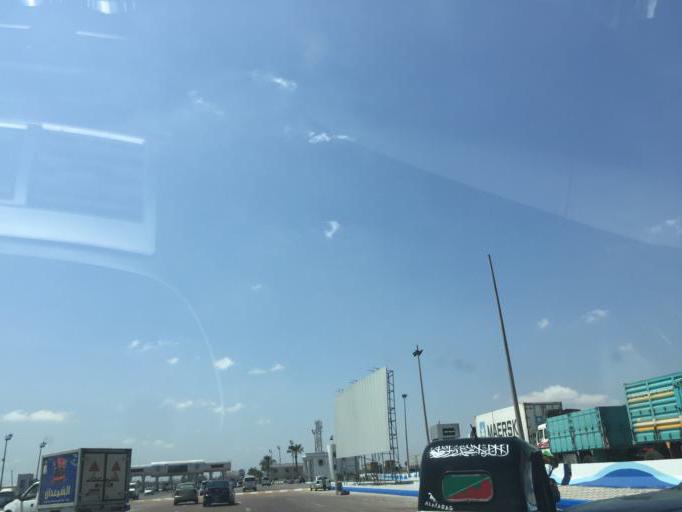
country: EG
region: Alexandria
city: Alexandria
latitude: 30.9677
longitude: 29.8295
